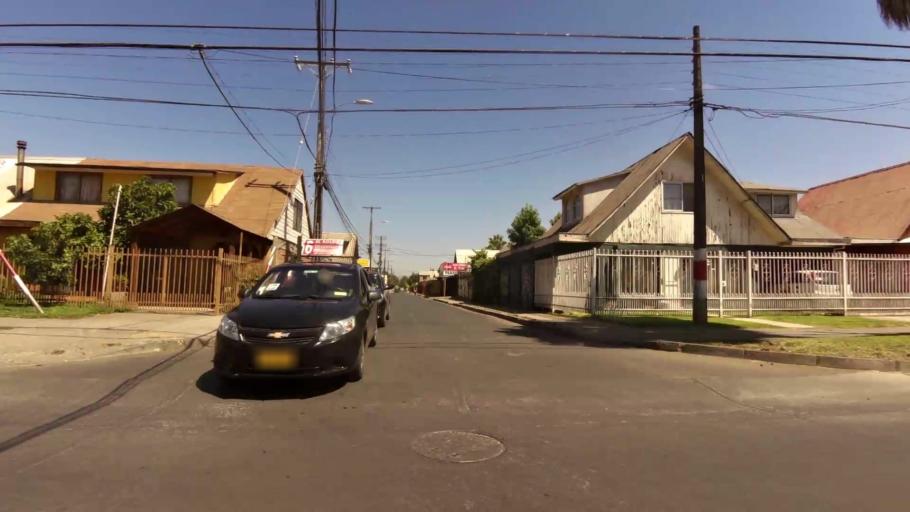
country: CL
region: Maule
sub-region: Provincia de Curico
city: Curico
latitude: -34.9686
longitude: -71.2304
